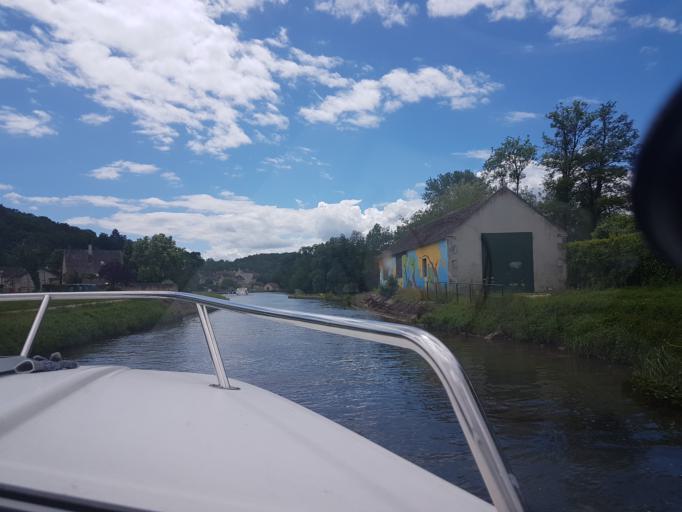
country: FR
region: Bourgogne
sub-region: Departement de l'Yonne
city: Vermenton
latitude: 47.6028
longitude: 3.6813
